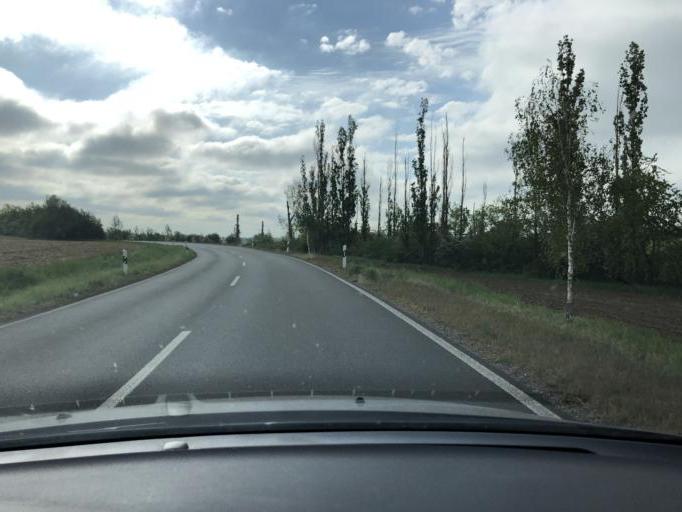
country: DE
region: Saxony
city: Neukieritzsch
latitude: 51.1544
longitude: 12.4238
